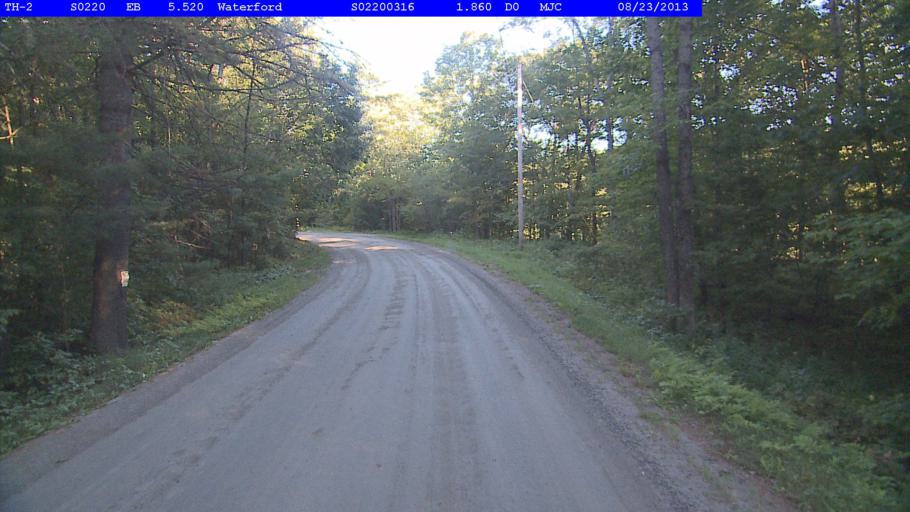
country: US
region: Vermont
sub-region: Caledonia County
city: Saint Johnsbury
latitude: 44.3384
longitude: -71.9650
